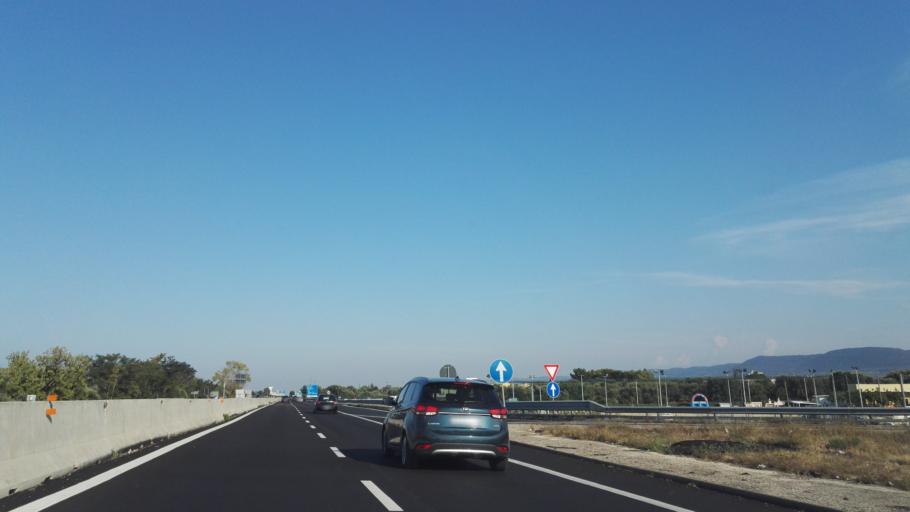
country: IT
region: Apulia
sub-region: Provincia di Brindisi
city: Fasano
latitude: 40.8399
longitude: 17.3740
